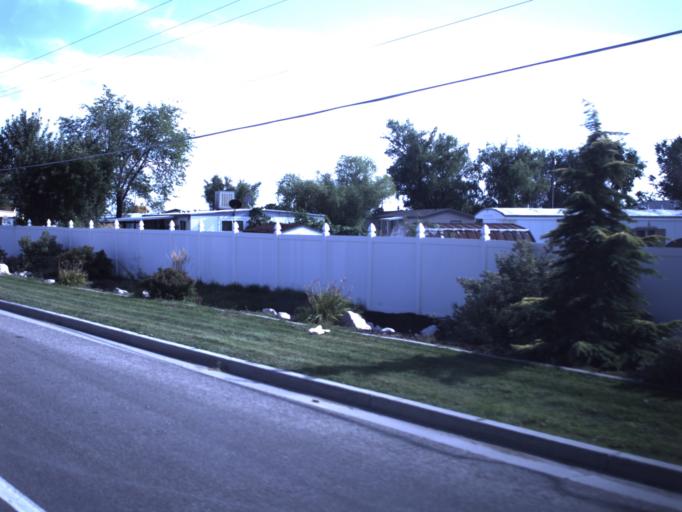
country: US
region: Utah
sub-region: Weber County
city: Pleasant View
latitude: 41.3028
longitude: -112.0020
